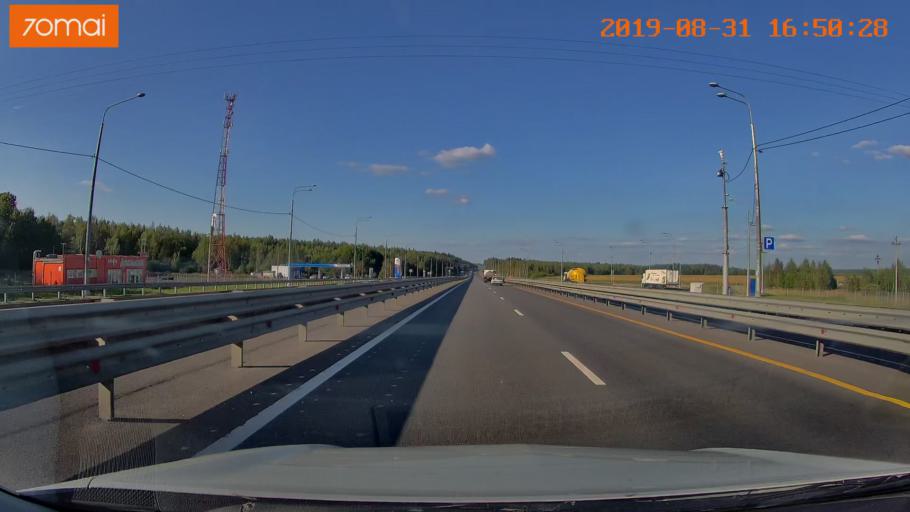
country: RU
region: Kaluga
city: Pyatovskiy
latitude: 54.7090
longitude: 36.1628
